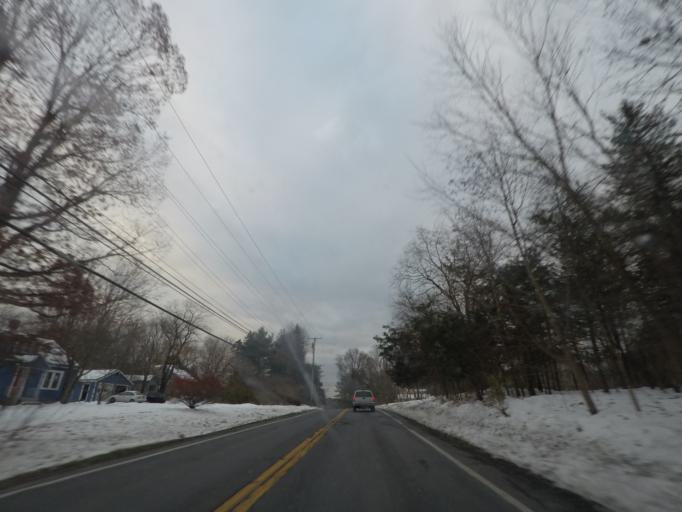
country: US
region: New York
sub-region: Ulster County
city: Plattekill
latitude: 41.5811
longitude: -74.0679
